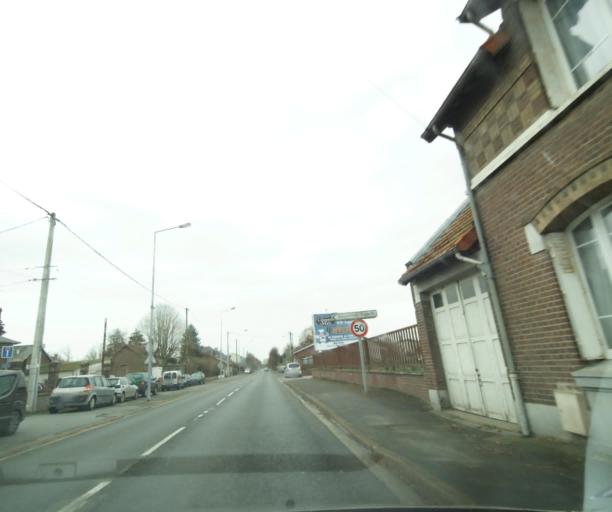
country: FR
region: Picardie
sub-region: Departement de l'Oise
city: Noyon
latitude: 49.5798
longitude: 3.0152
